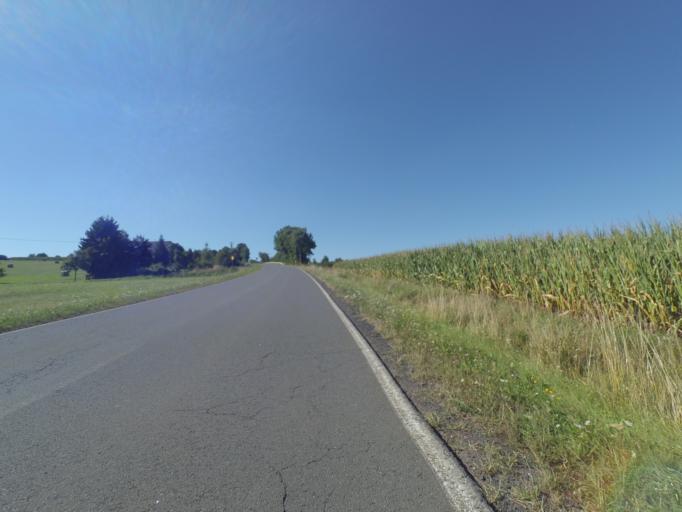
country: DE
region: Rheinland-Pfalz
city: Strotzbusch
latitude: 50.1077
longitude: 6.9453
